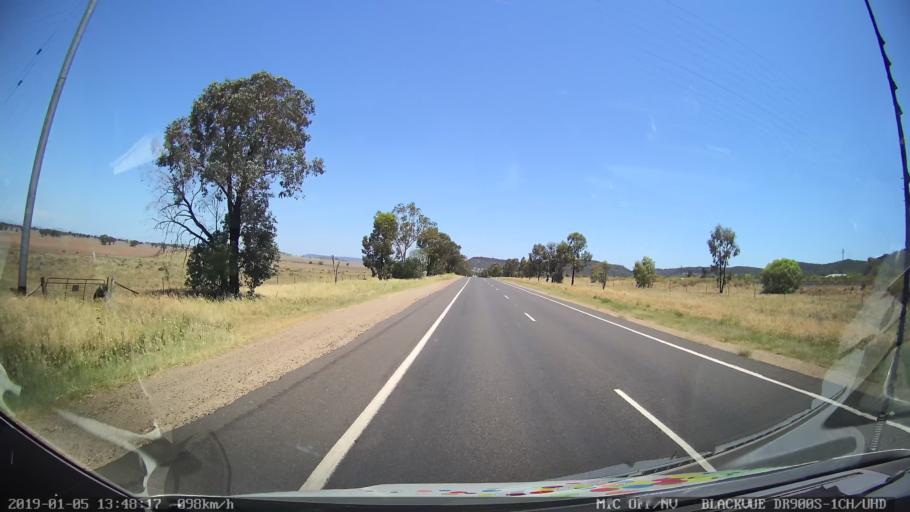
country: AU
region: New South Wales
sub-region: Gunnedah
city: Gunnedah
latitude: -30.9996
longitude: 150.2788
